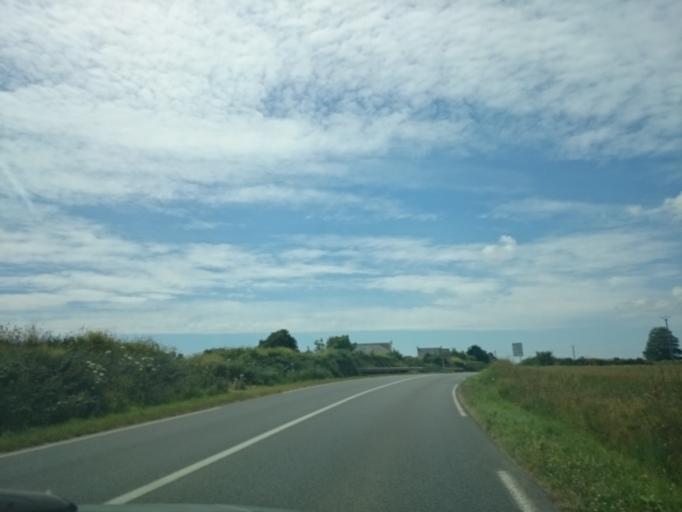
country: FR
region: Brittany
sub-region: Departement du Finistere
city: Plouzane
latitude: 48.3616
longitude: -4.6124
